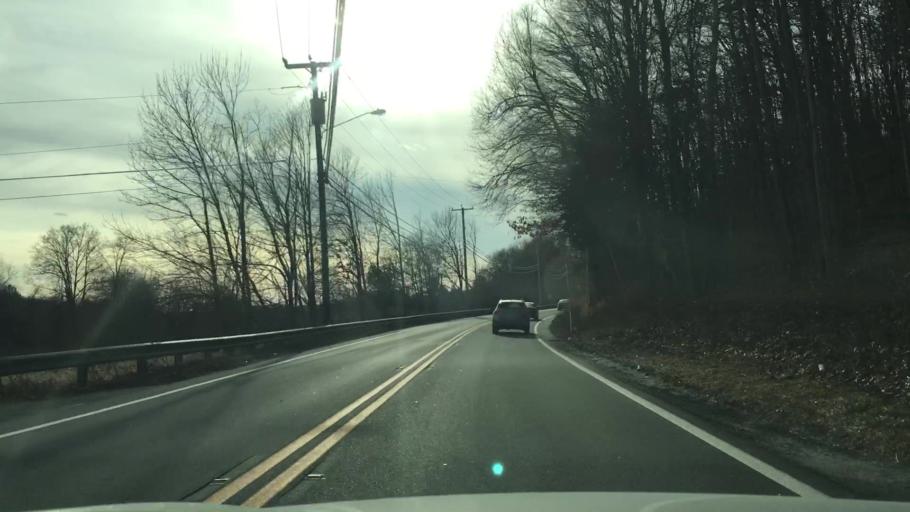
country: US
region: Massachusetts
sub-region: Hampden County
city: Southwick
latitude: 42.0498
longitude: -72.7765
